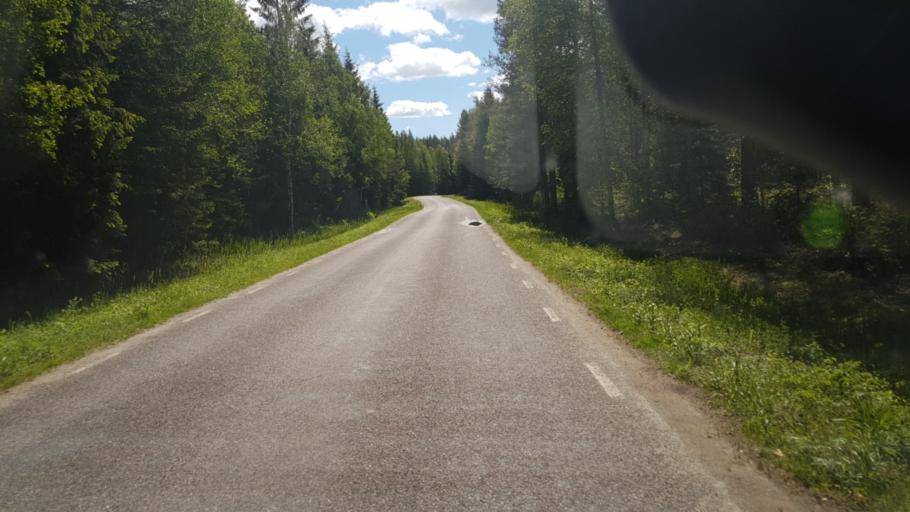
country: SE
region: Vaermland
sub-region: Grums Kommun
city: Slottsbron
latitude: 59.4927
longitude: 12.8807
